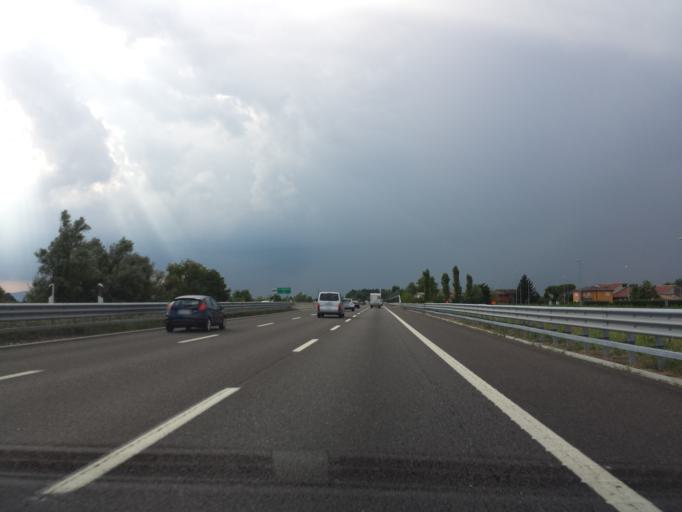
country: IT
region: Veneto
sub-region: Provincia di Padova
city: Ronchi di Campanile
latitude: 45.4622
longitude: 11.7717
